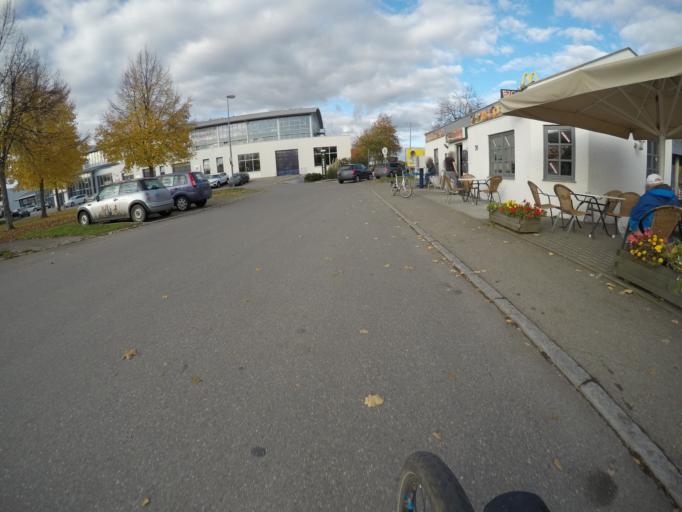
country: DE
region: Baden-Wuerttemberg
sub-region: Regierungsbezirk Stuttgart
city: Filderstadt
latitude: 48.6769
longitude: 9.1957
